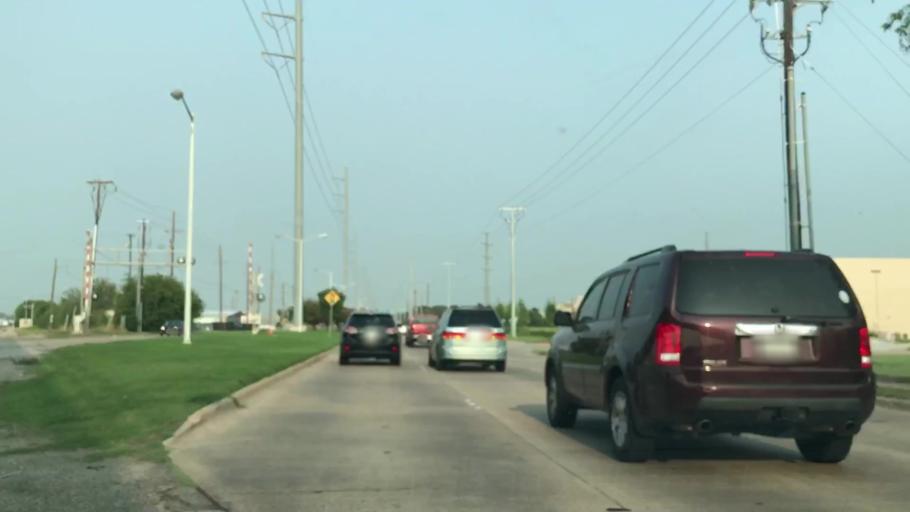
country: US
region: Texas
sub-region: Dallas County
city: Garland
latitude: 32.9091
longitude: -96.6755
